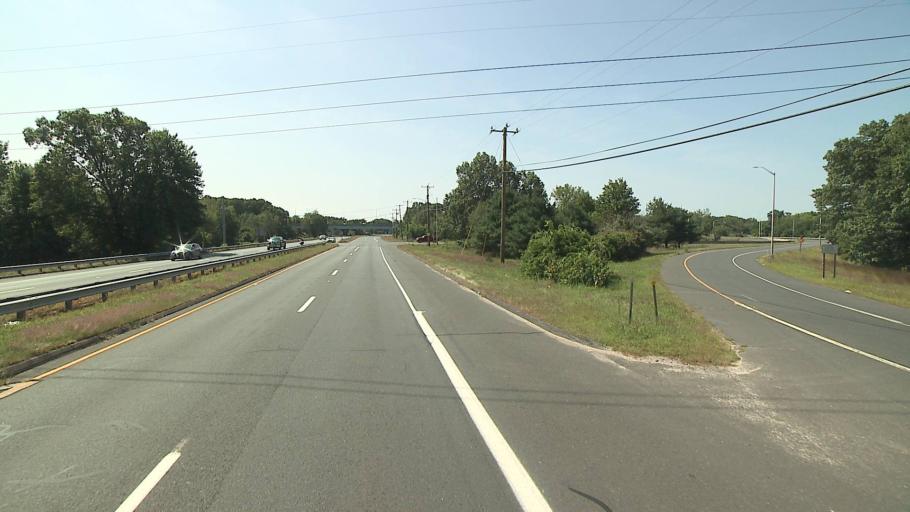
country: US
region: Connecticut
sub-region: Hartford County
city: South Windsor
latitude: 41.8085
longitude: -72.6136
